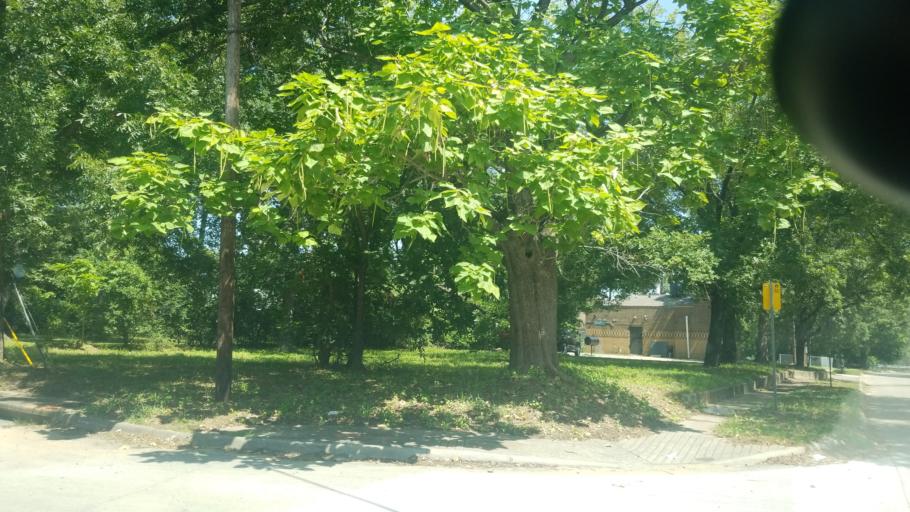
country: US
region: Texas
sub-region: Dallas County
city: Hutchins
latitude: 32.7133
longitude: -96.7444
